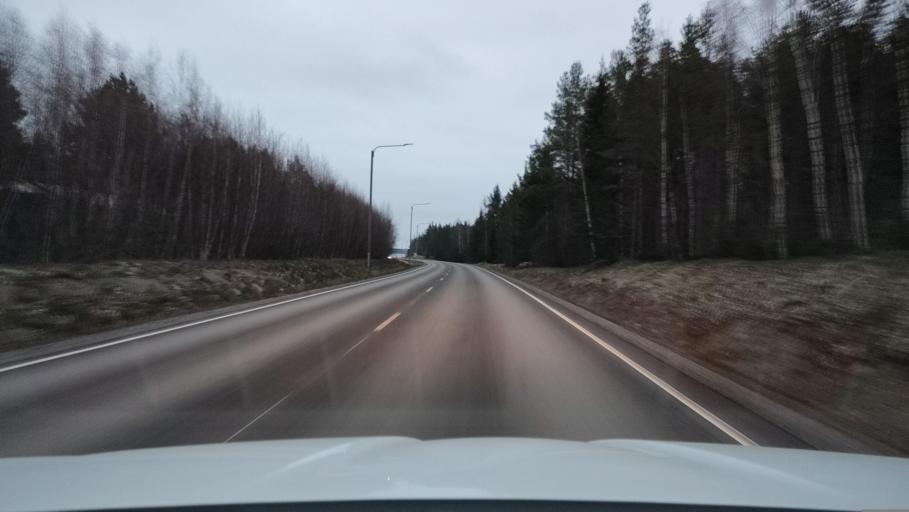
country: FI
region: Ostrobothnia
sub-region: Vaasa
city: Replot
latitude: 63.2077
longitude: 21.4437
